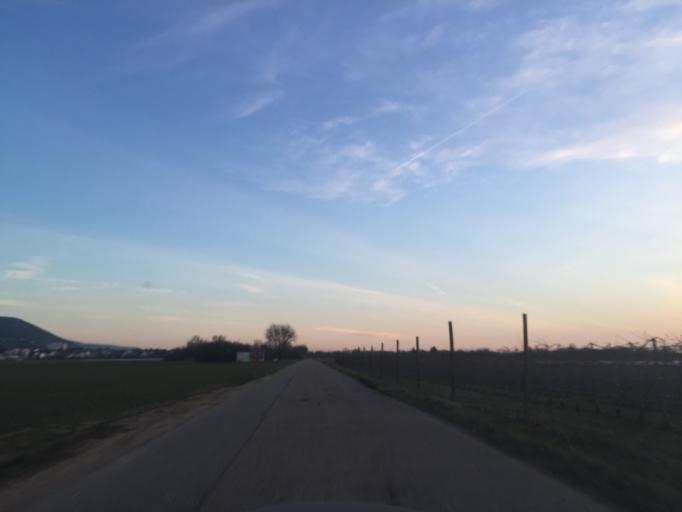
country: DE
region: Baden-Wuerttemberg
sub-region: Karlsruhe Region
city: Schriesheim
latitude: 49.5078
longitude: 8.6476
